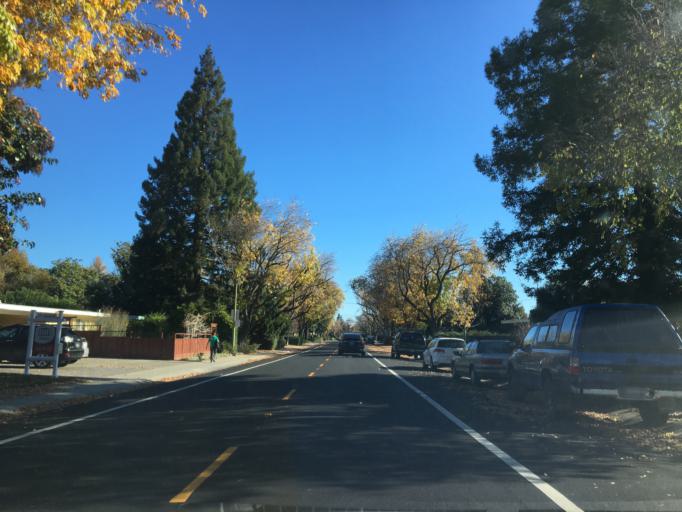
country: US
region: California
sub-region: Santa Clara County
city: Palo Alto
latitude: 37.4288
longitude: -122.1096
